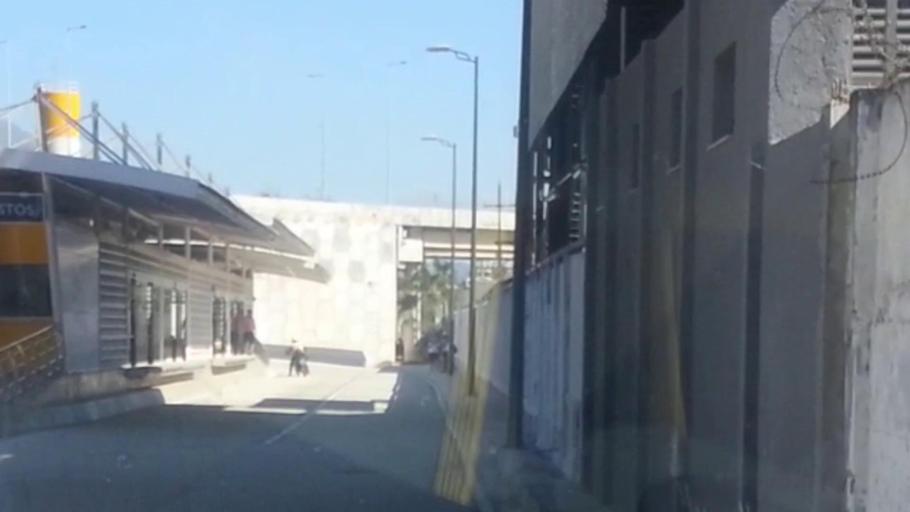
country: BR
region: Rio de Janeiro
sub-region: Nilopolis
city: Nilopolis
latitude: -22.8654
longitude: -43.4078
